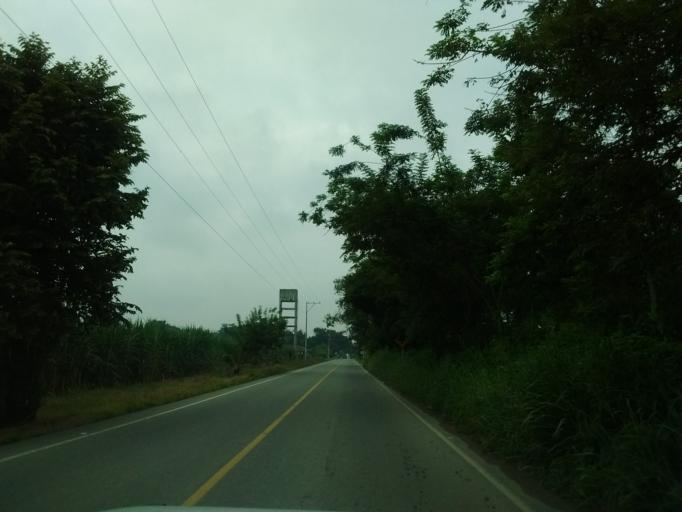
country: CO
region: Cauca
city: Padilla
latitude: 3.2256
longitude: -76.3554
